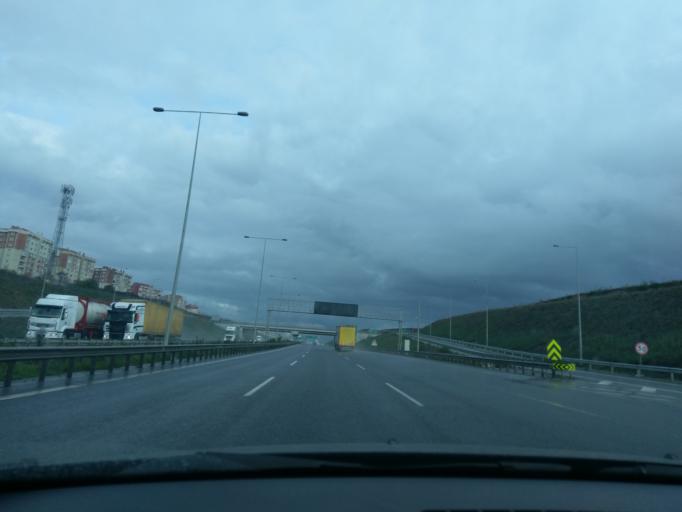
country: TR
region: Istanbul
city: Basaksehir
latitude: 41.0900
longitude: 28.8138
